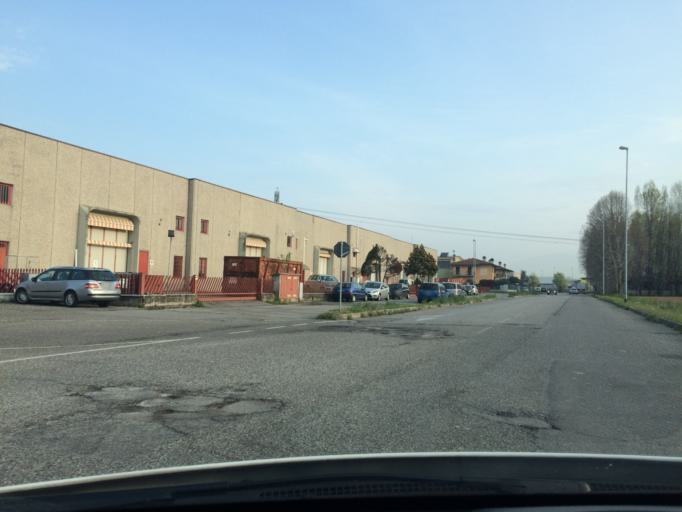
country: IT
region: Lombardy
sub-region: Provincia di Brescia
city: Flero
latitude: 45.4884
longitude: 10.1652
